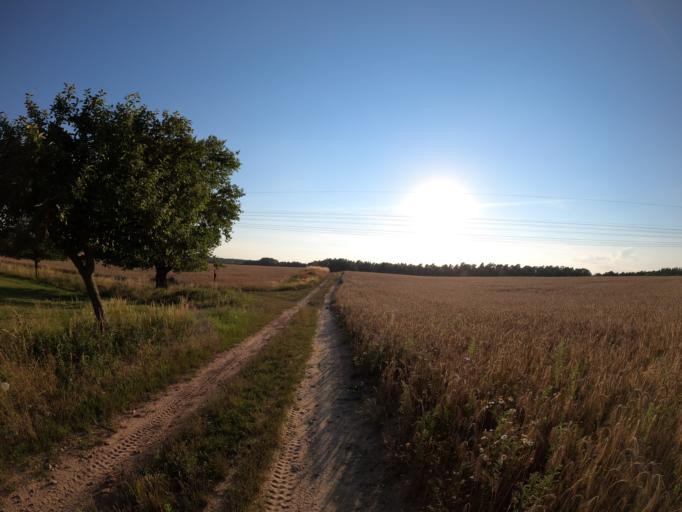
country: DE
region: Brandenburg
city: Althuttendorf
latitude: 53.0350
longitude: 13.8678
